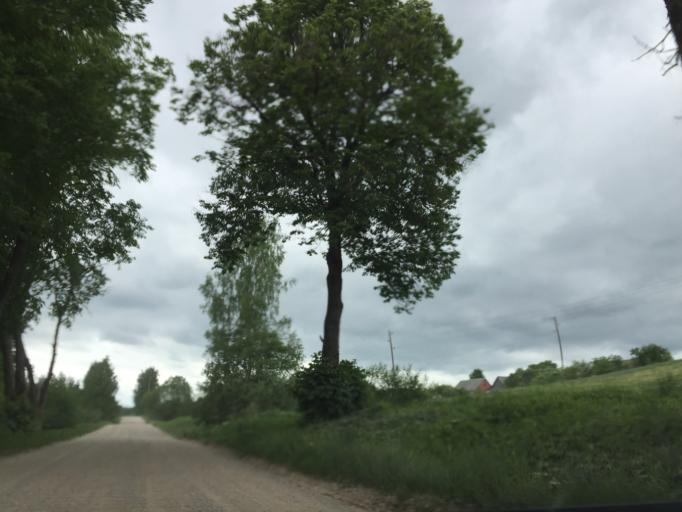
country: LV
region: Dagda
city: Dagda
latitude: 56.1864
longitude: 27.6453
